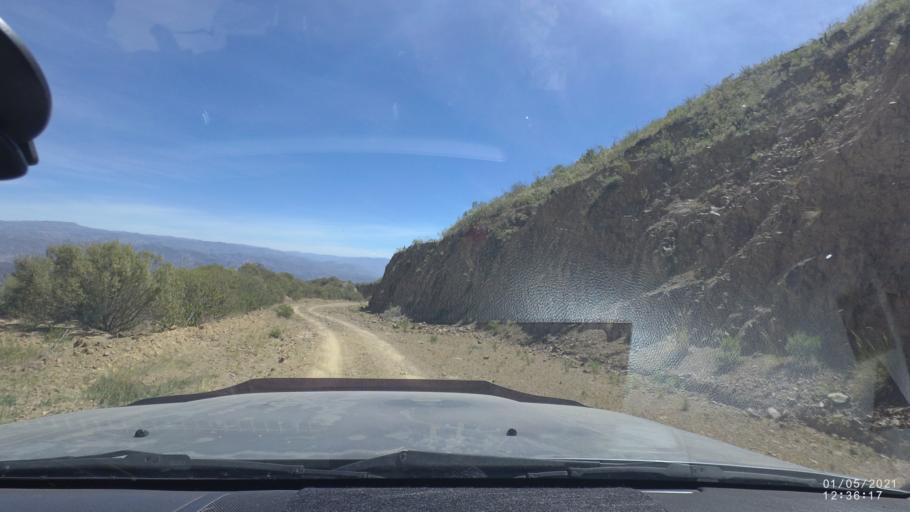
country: BO
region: Cochabamba
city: Capinota
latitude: -17.6783
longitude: -66.1554
